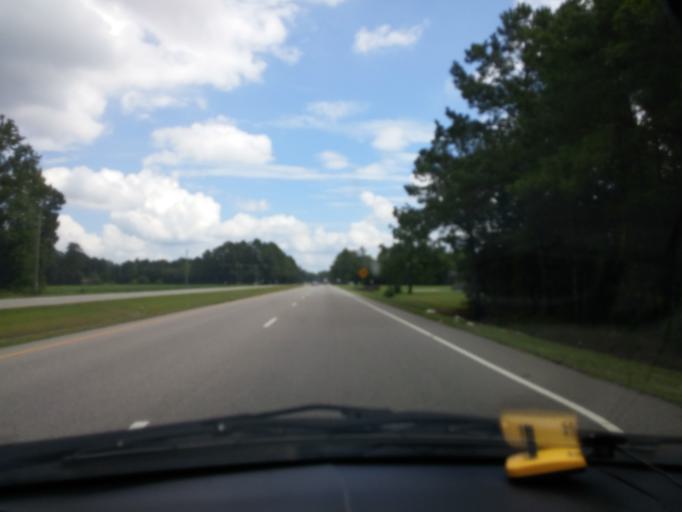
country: US
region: North Carolina
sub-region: Pitt County
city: Grifton
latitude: 35.3238
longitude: -77.5044
